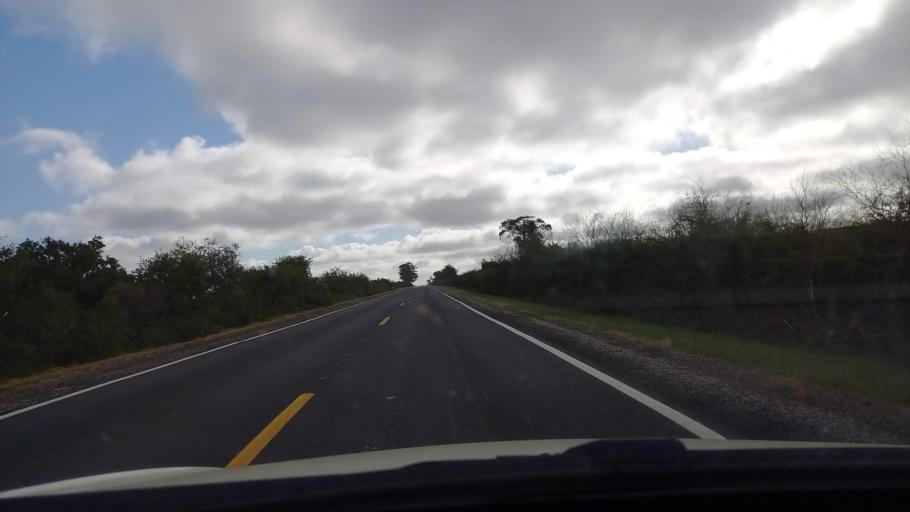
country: BR
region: Rio Grande do Sul
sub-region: Dom Pedrito
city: Dom Pedrito
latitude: -30.8951
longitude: -54.8498
